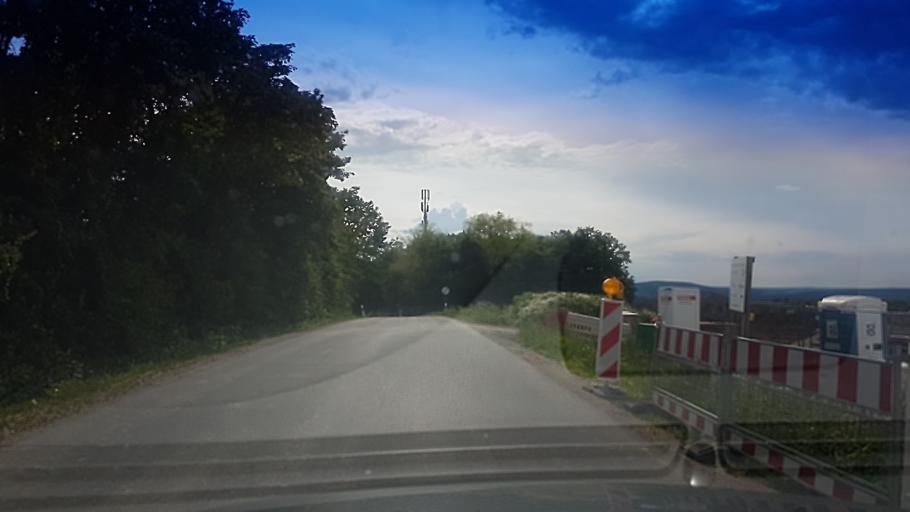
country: DE
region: Bavaria
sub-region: Upper Franconia
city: Hirschaid
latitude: 49.8336
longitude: 11.0159
